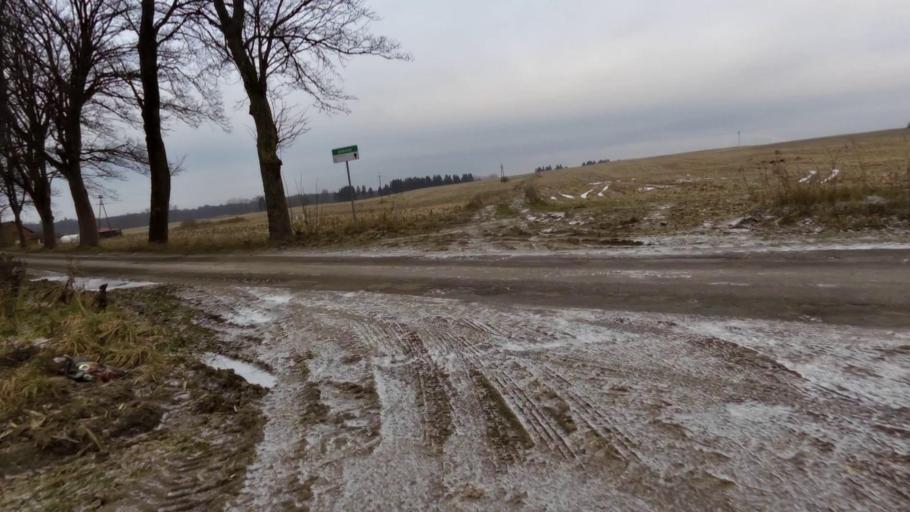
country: PL
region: West Pomeranian Voivodeship
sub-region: Powiat szczecinecki
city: Szczecinek
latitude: 53.6546
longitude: 16.6333
